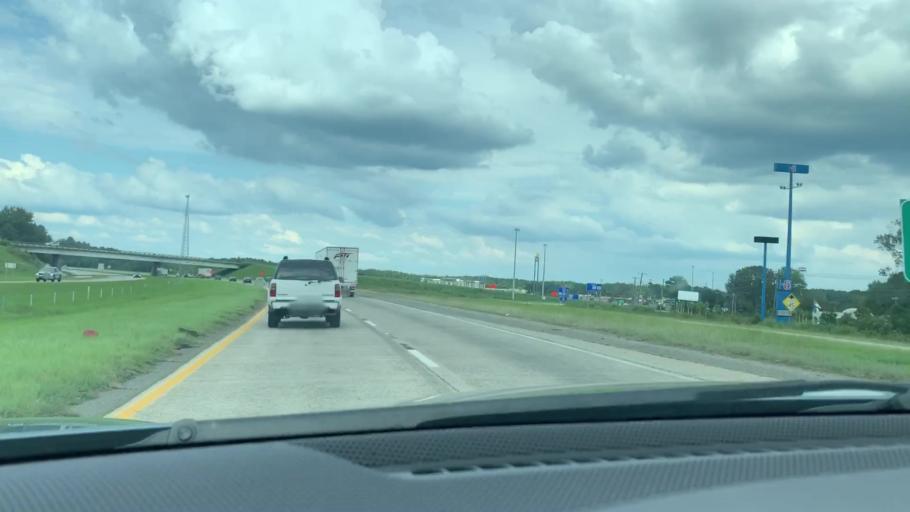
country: US
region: South Carolina
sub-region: Hampton County
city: Yemassee
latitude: 32.6285
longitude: -80.8831
